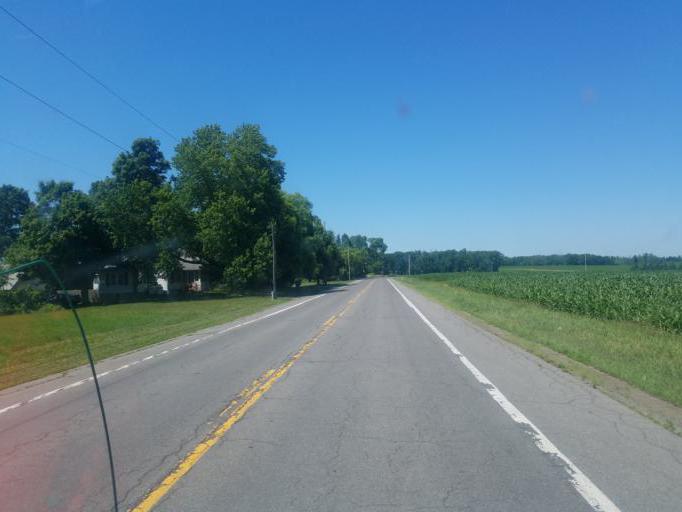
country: US
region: New York
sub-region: Ontario County
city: Geneva
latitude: 42.8387
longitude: -77.0377
